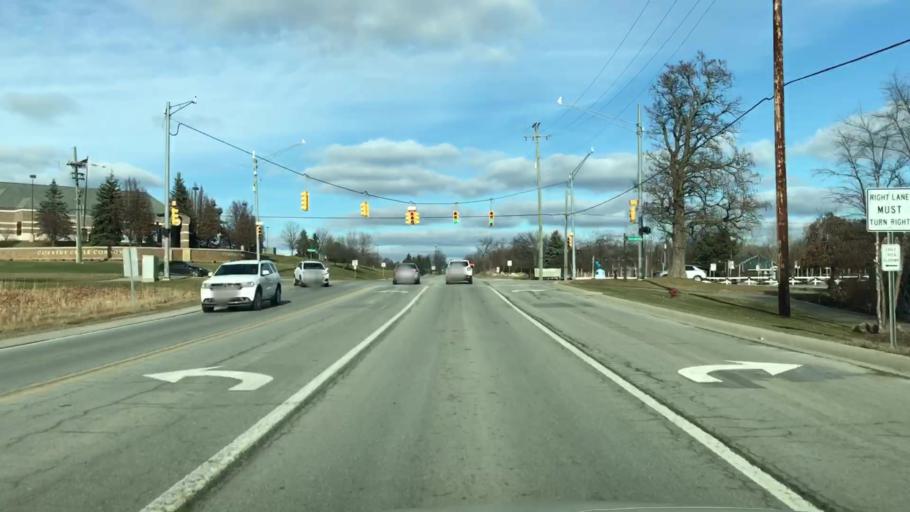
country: US
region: Michigan
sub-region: Oakland County
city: Auburn Hills
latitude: 42.7232
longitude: -83.1962
